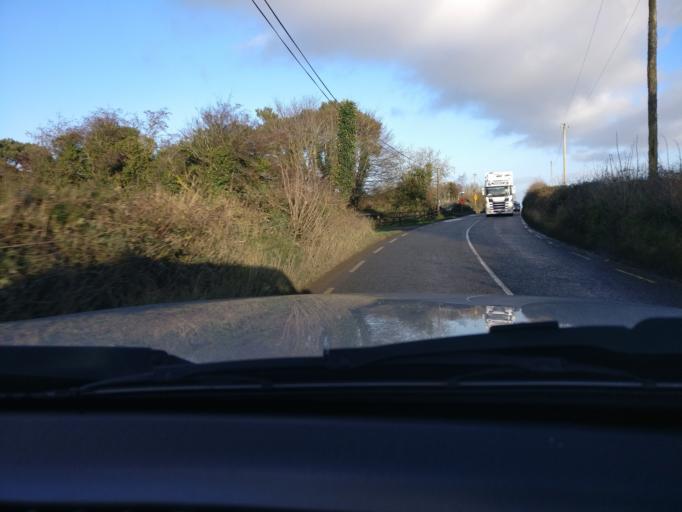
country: IE
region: Ulster
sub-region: An Cabhan
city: Mullagh
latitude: 53.7239
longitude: -6.9950
